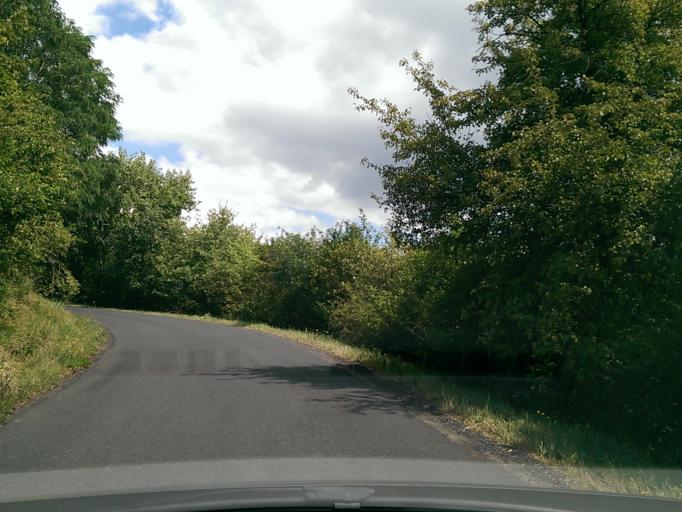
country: CZ
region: Ustecky
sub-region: Okres Litomerice
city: Steti
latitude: 50.5076
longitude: 14.4135
